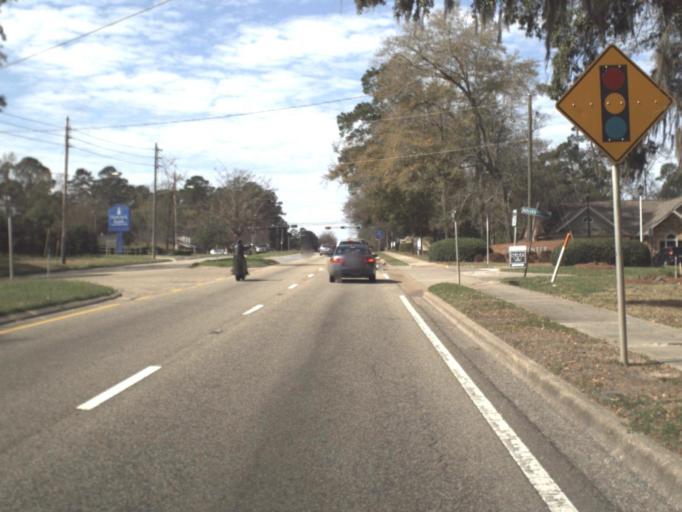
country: US
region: Florida
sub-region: Leon County
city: Tallahassee
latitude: 30.4578
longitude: -84.2346
